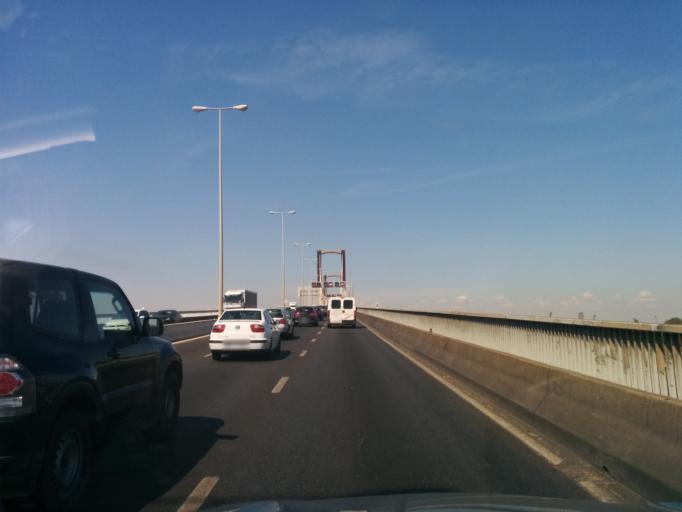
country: ES
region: Andalusia
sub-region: Provincia de Sevilla
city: Gelves
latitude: 37.3441
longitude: -5.9872
